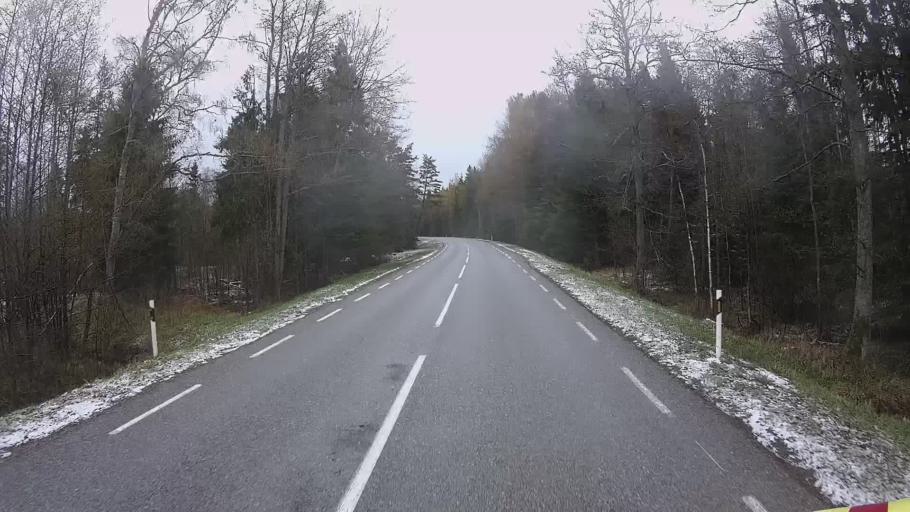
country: EE
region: Hiiumaa
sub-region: Kaerdla linn
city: Kardla
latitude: 59.0342
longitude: 22.6794
